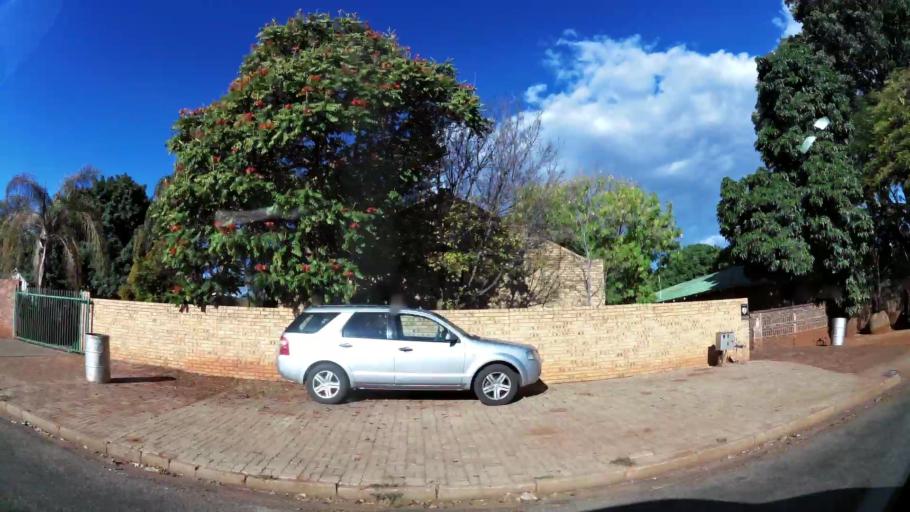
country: ZA
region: Limpopo
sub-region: Waterberg District Municipality
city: Mokopane
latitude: -24.1926
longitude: 29.0052
